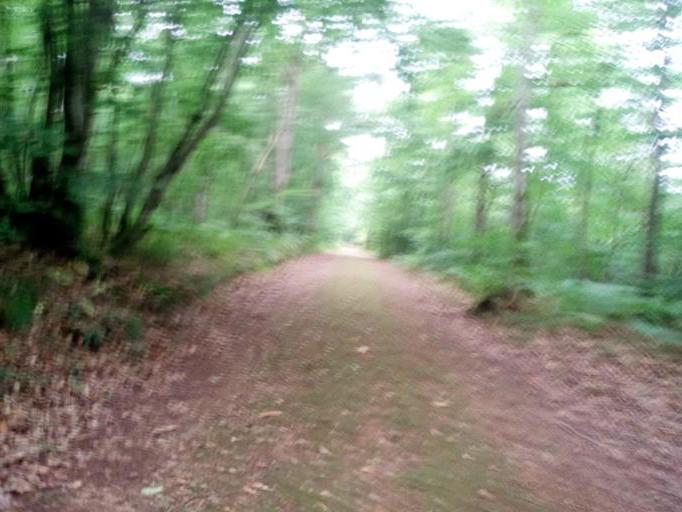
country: FR
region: Lower Normandy
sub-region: Departement du Calvados
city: Clinchamps-sur-Orne
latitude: 49.0397
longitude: -0.4365
